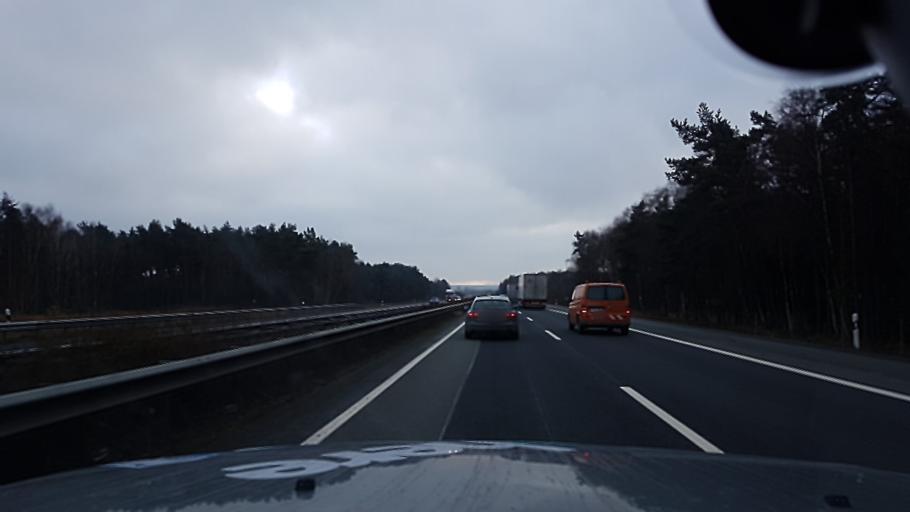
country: DE
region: Lower Saxony
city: Rieste
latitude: 52.4304
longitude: 8.0320
